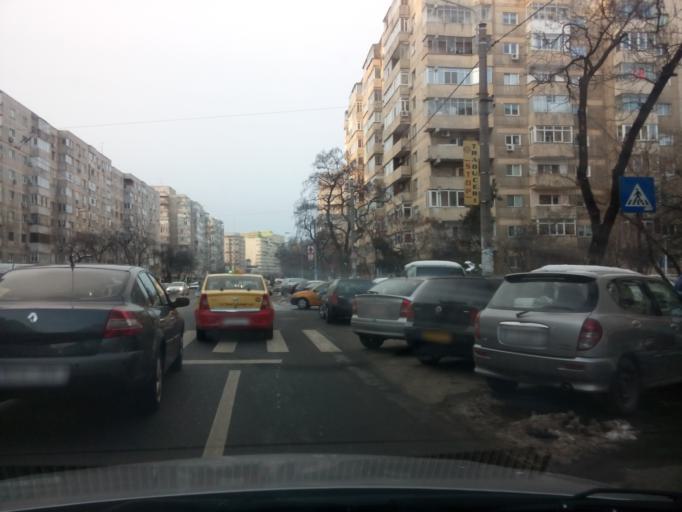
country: RO
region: Ilfov
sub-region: Comuna Fundeni-Dobroesti
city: Fundeni
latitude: 44.4380
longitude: 26.1589
